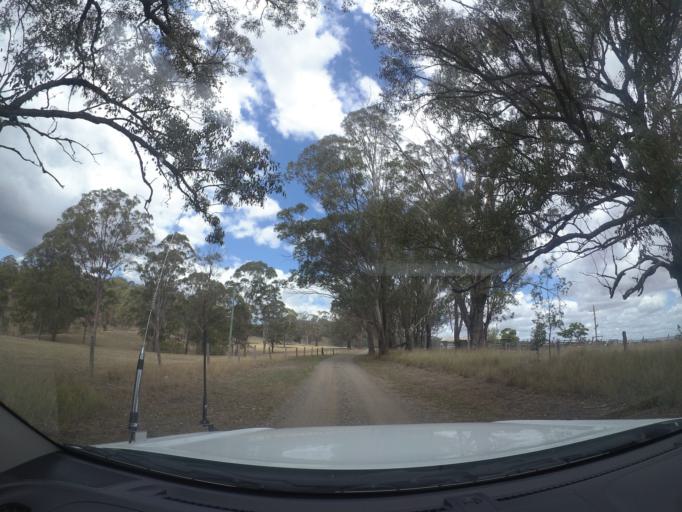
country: AU
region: Queensland
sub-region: Logan
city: Cedar Vale
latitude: -27.9160
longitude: 153.0312
